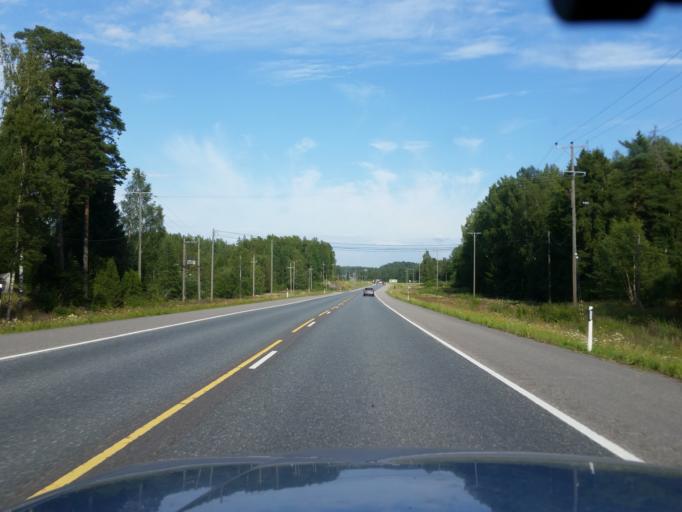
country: FI
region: Uusimaa
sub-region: Helsinki
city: Siuntio
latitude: 60.0921
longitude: 24.2240
